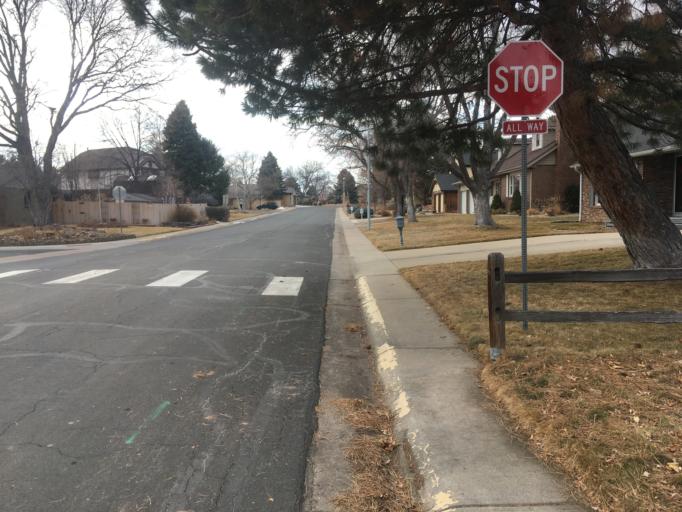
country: US
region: Colorado
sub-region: Broomfield County
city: Broomfield
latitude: 39.9384
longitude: -105.0595
